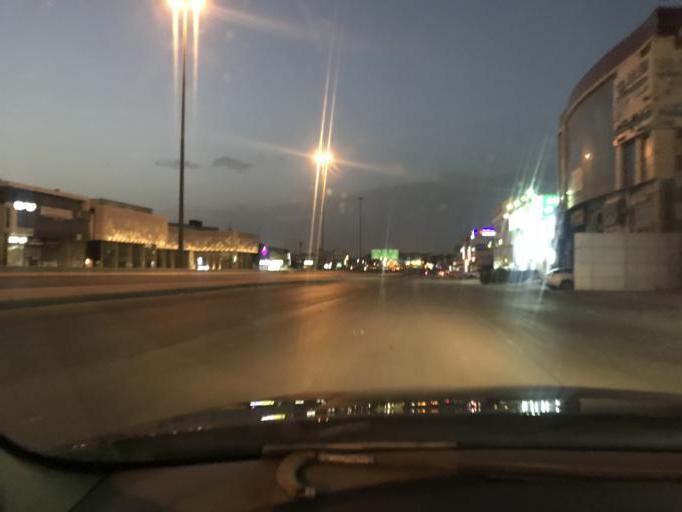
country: SA
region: Ar Riyad
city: Riyadh
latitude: 24.7944
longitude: 46.7000
